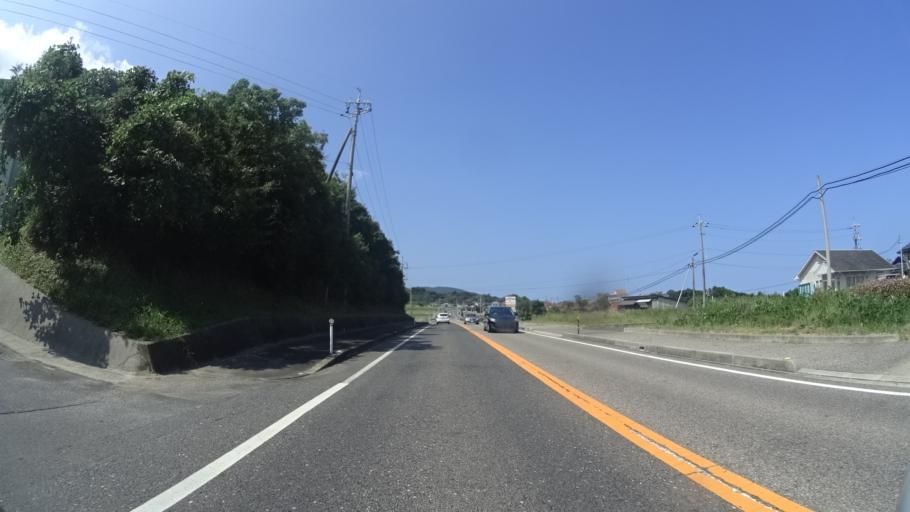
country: JP
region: Shimane
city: Masuda
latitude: 34.6710
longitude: 131.7454
